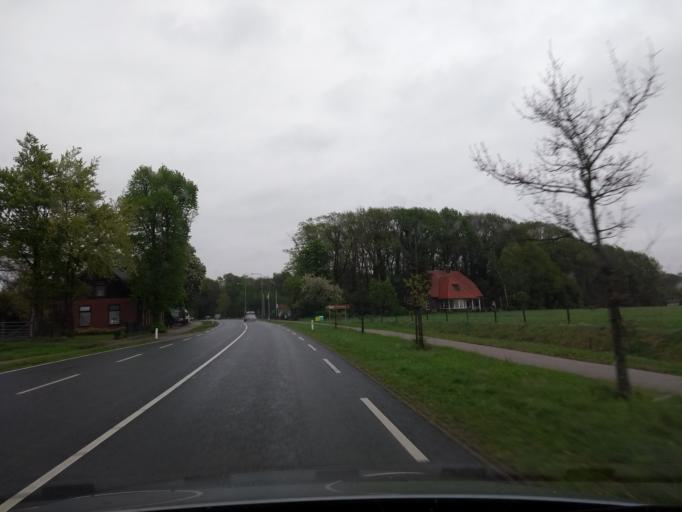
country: DE
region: Lower Saxony
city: Getelo
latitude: 52.3999
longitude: 6.8559
